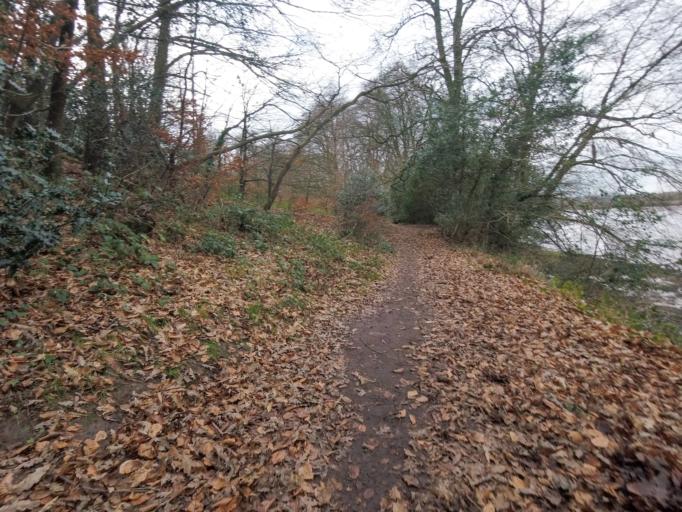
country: IE
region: Munster
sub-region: Waterford
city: Waterford
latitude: 52.2528
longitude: -7.0797
